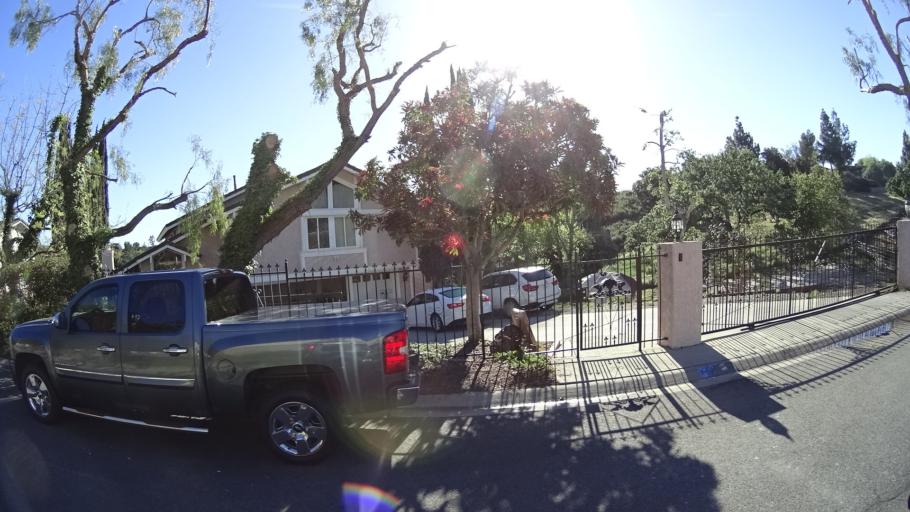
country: US
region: California
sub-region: Ventura County
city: Casa Conejo
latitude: 34.1875
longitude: -118.9042
